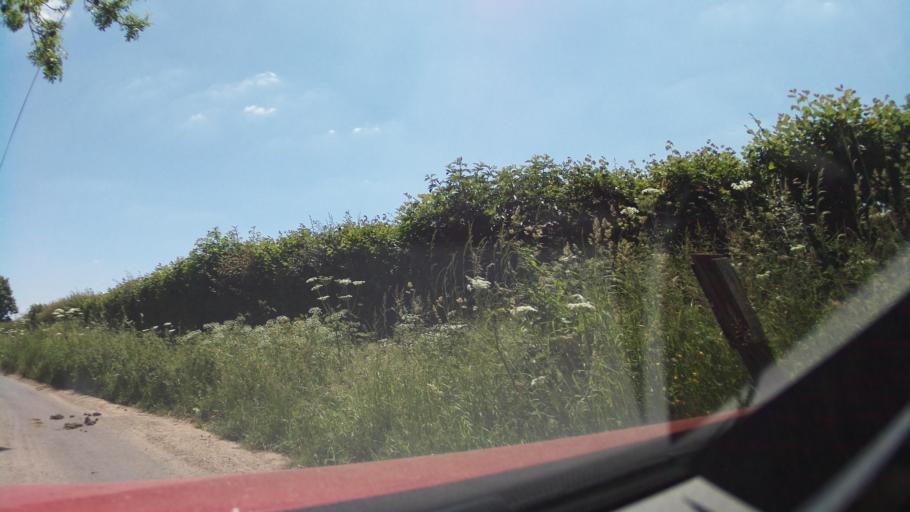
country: GB
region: England
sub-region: Wiltshire
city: Bremhill
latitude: 51.4656
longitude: -2.0741
